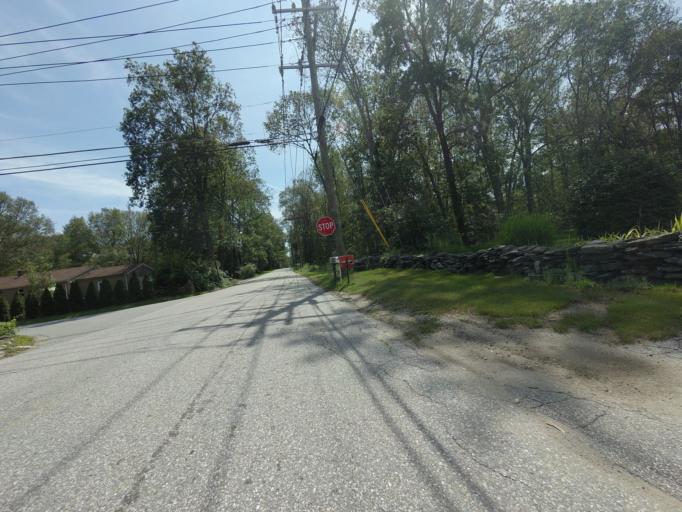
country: US
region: Connecticut
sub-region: Windham County
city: East Brooklyn
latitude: 41.8166
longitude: -71.9234
